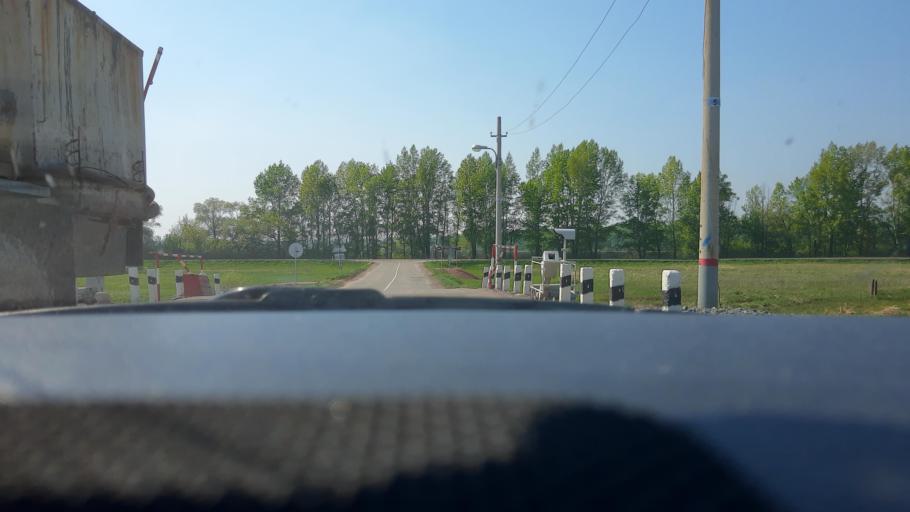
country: RU
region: Bashkortostan
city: Chishmy
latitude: 54.4502
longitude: 55.2500
